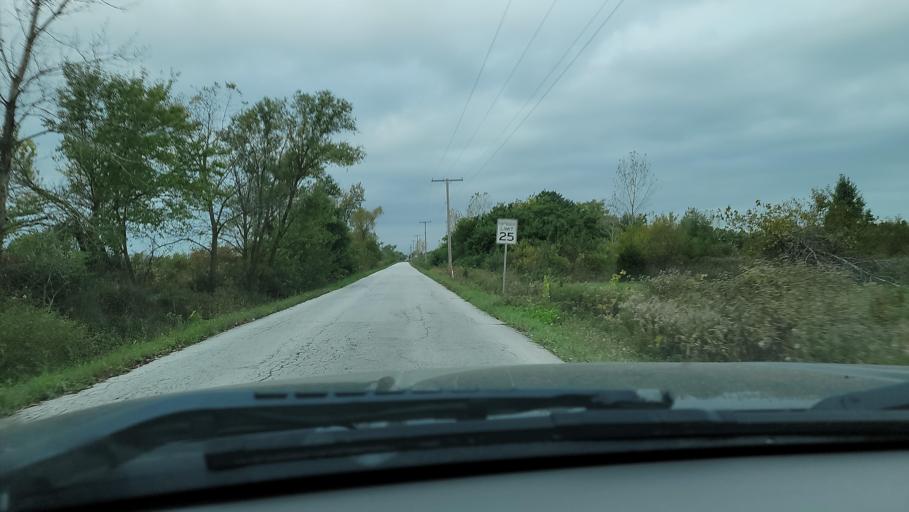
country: US
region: Indiana
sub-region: Porter County
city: South Haven
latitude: 41.5613
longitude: -87.1533
